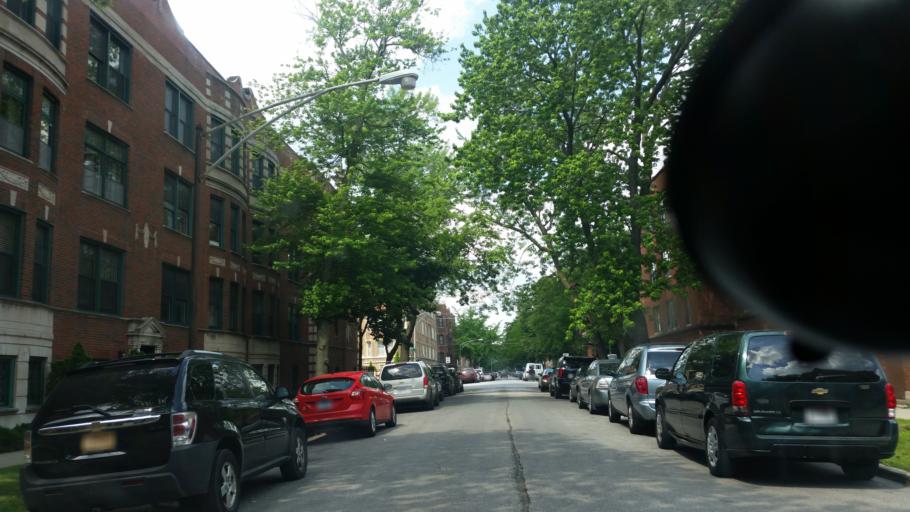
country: US
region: Illinois
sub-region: Cook County
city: Chicago
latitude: 41.7717
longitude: -87.5708
